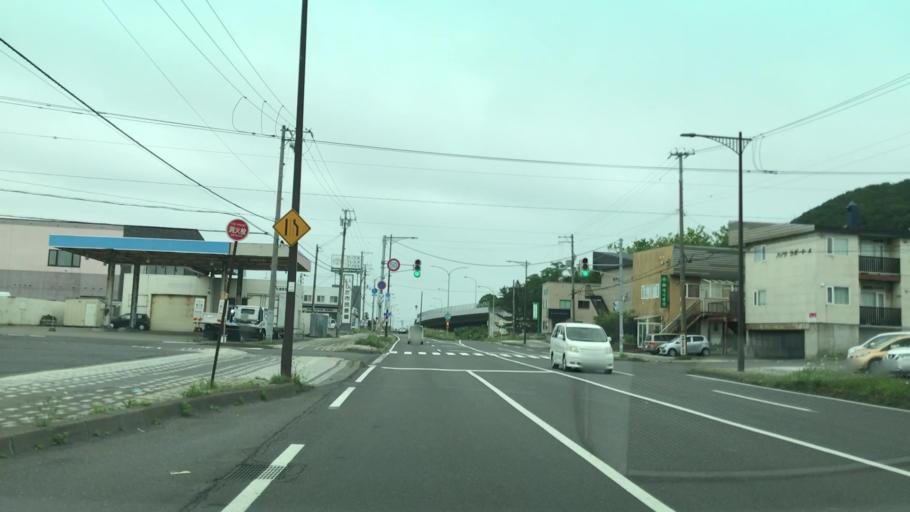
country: JP
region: Hokkaido
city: Muroran
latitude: 42.3522
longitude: 141.0429
